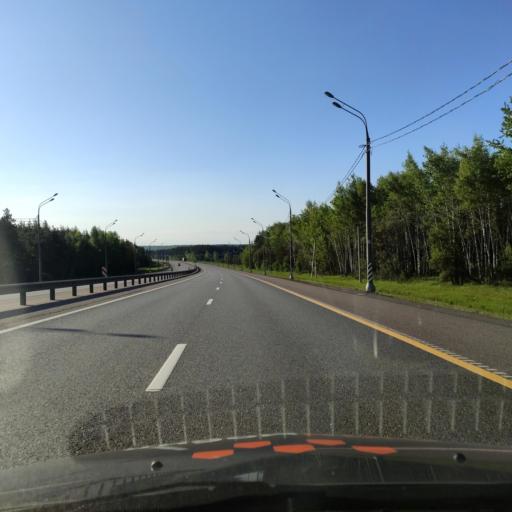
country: RU
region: Lipetsk
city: Zadonsk
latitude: 52.3823
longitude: 38.8747
